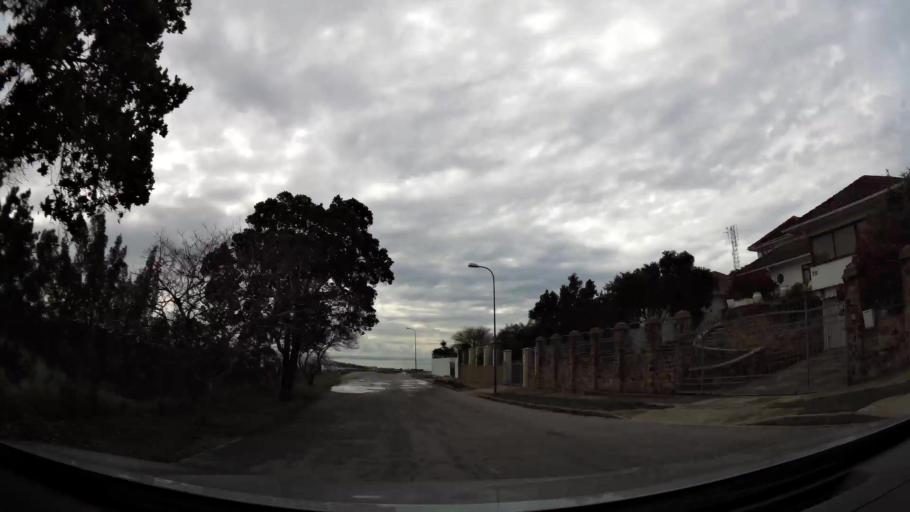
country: ZA
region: Eastern Cape
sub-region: Nelson Mandela Bay Metropolitan Municipality
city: Port Elizabeth
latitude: -33.9492
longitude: 25.5954
